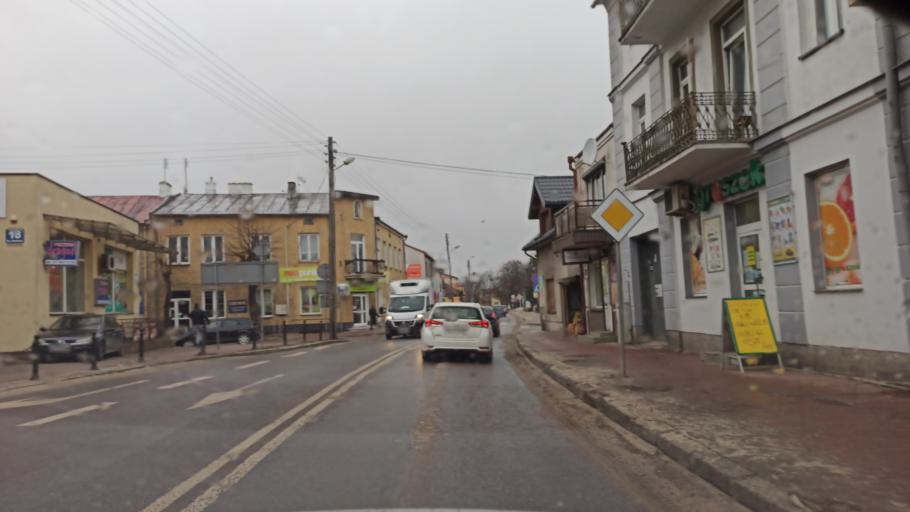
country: PL
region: Lublin Voivodeship
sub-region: Powiat lubelski
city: Bychawa
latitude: 51.0150
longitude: 22.5349
